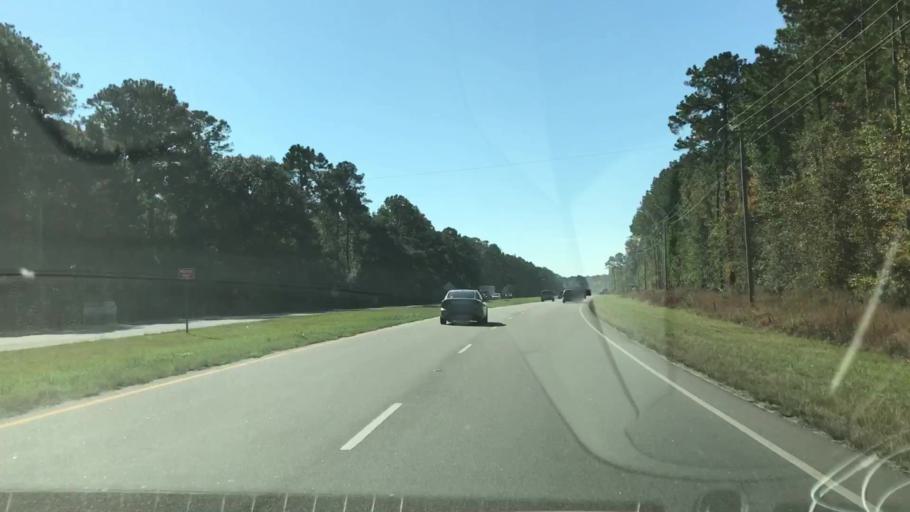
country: US
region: South Carolina
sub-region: Beaufort County
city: Bluffton
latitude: 32.3306
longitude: -80.9291
